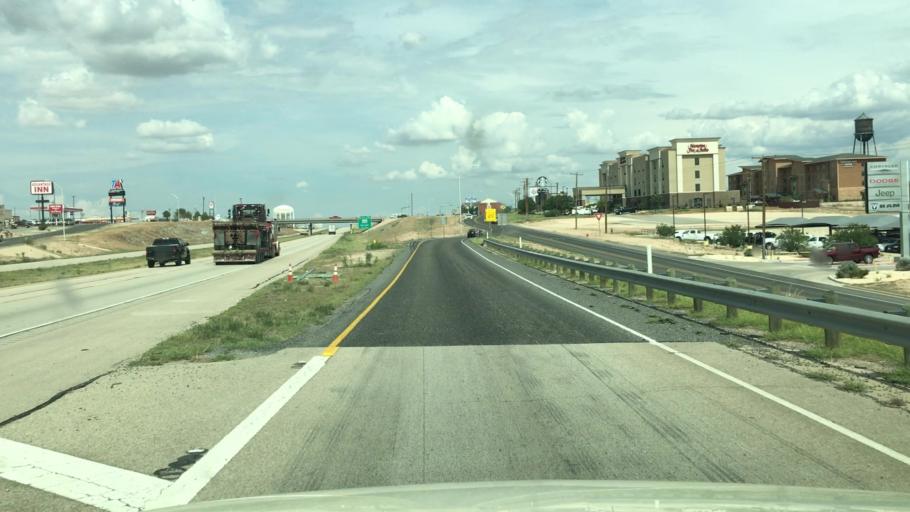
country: US
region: Texas
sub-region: Howard County
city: Big Spring
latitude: 32.2624
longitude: -101.4950
